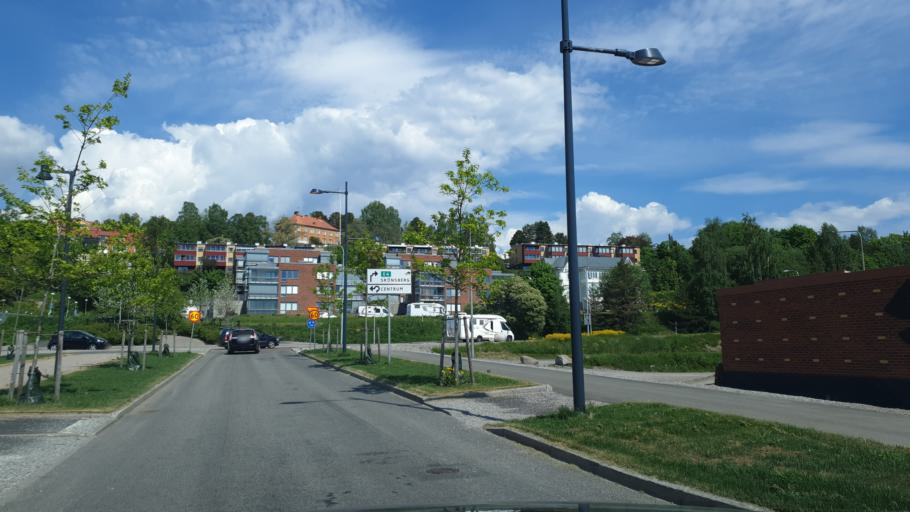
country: SE
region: Vaesternorrland
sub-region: Sundsvalls Kommun
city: Sundsvall
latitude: 62.3945
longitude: 17.3283
